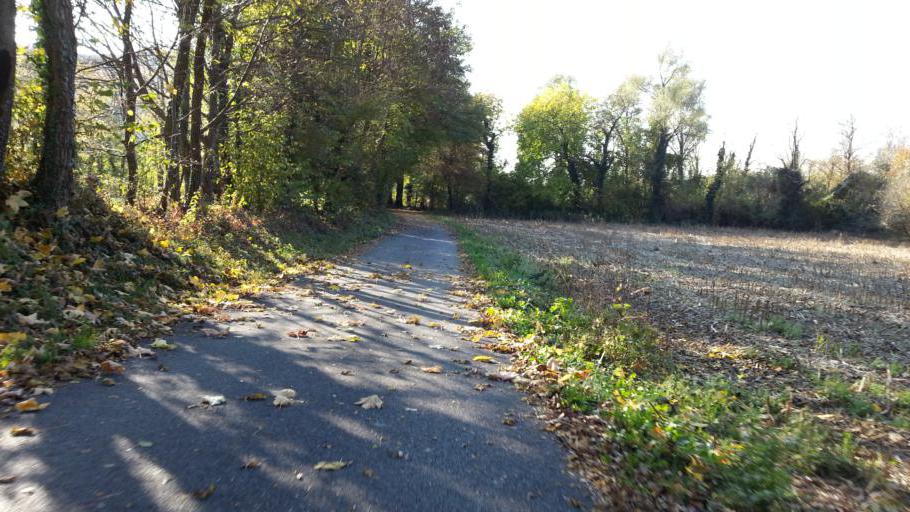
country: IT
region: Friuli Venezia Giulia
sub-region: Provincia di Udine
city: Venzone
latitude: 46.3224
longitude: 13.1280
